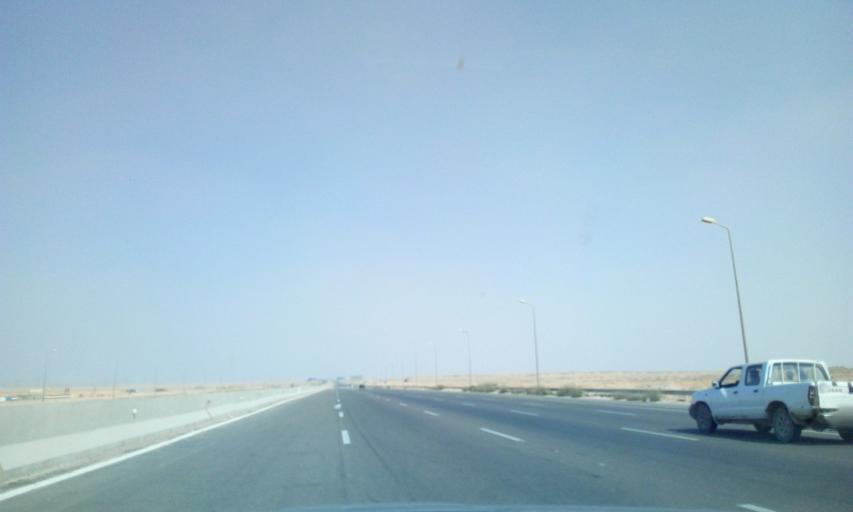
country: EG
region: Muhafazat al Qahirah
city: Halwan
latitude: 29.9041
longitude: 31.7524
